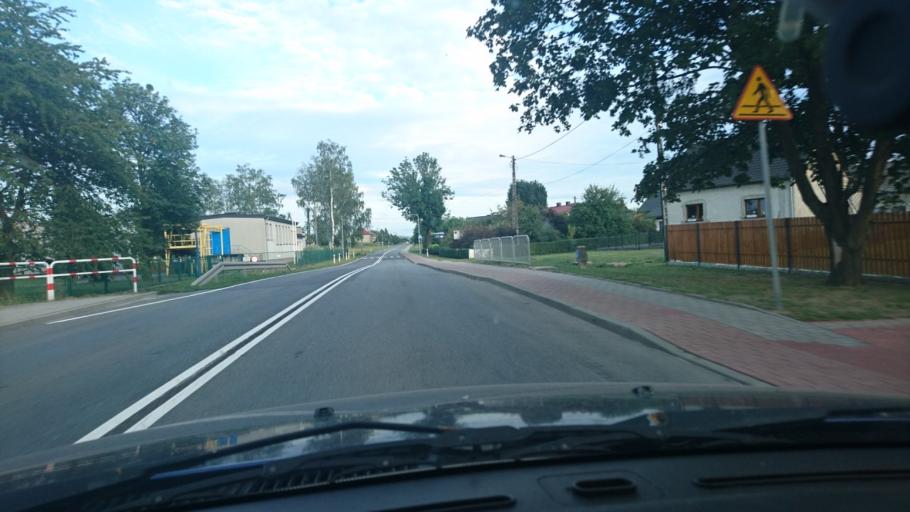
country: PL
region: Opole Voivodeship
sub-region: Powiat oleski
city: Olesno
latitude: 50.8728
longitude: 18.4285
